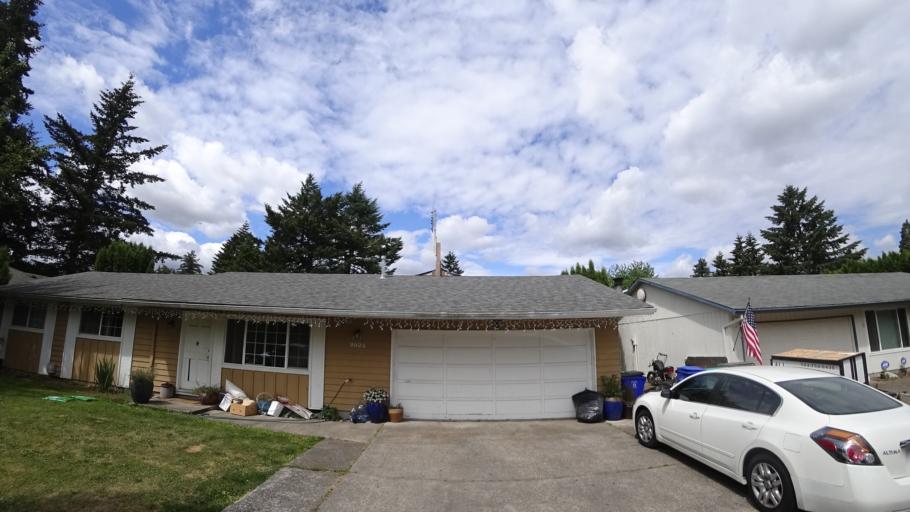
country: US
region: Oregon
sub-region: Multnomah County
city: Lents
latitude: 45.4942
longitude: -122.5288
